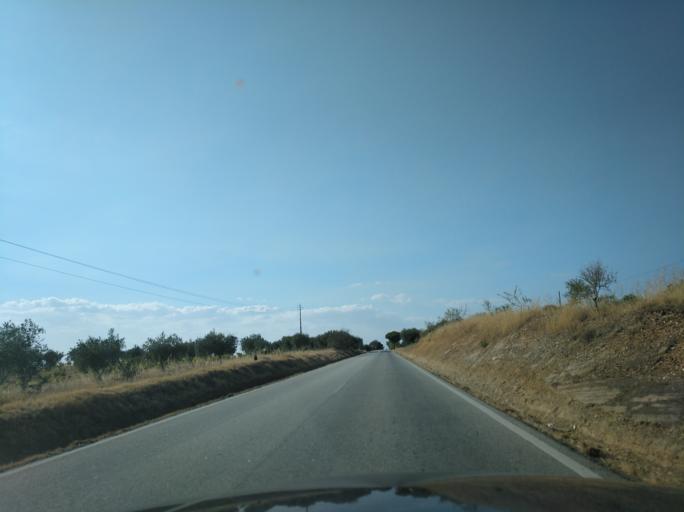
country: ES
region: Extremadura
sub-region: Provincia de Badajoz
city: Valencia del Mombuey
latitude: 38.2305
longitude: -7.2326
